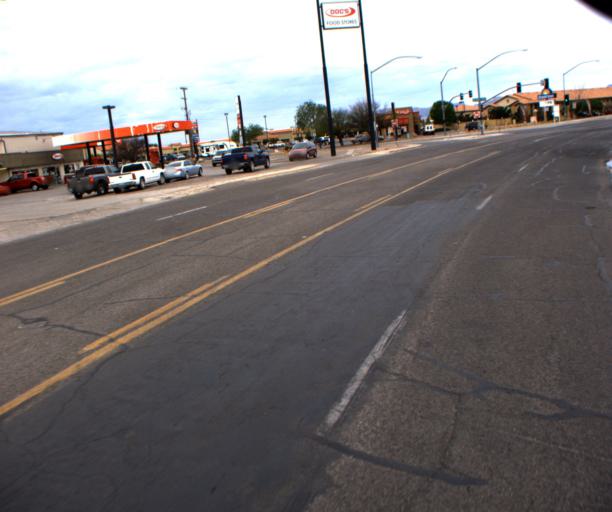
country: US
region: Arizona
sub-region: Cochise County
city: Willcox
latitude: 32.2643
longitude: -109.8404
